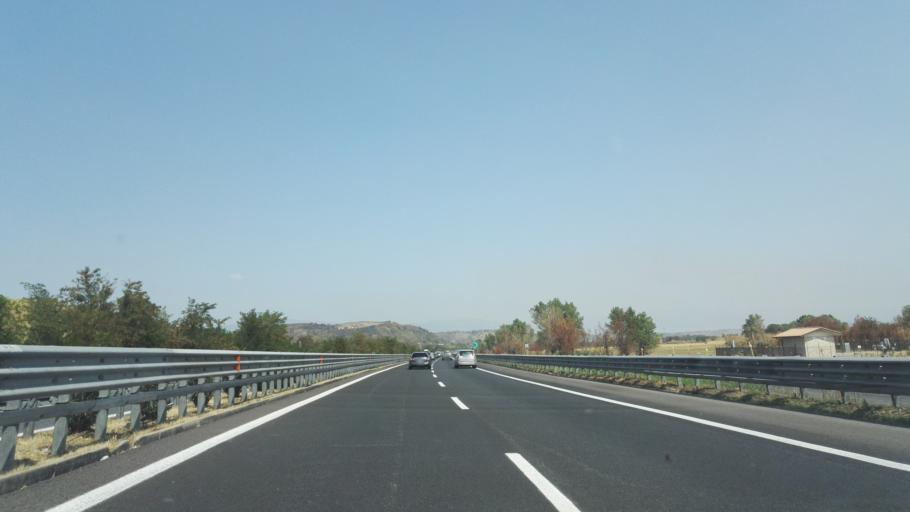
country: IT
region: Calabria
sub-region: Provincia di Cosenza
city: Taverna
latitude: 39.4662
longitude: 16.2203
